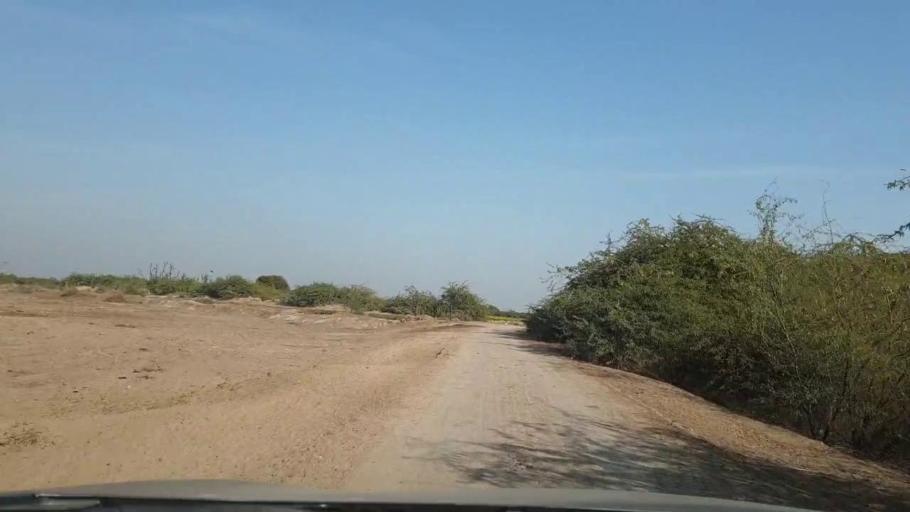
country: PK
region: Sindh
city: Berani
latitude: 25.7270
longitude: 68.7886
